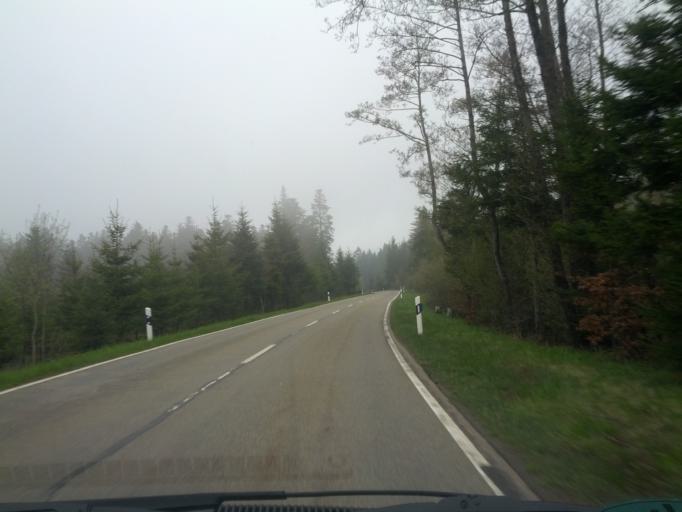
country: DE
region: Baden-Wuerttemberg
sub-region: Freiburg Region
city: Rickenbach
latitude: 47.6055
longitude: 8.0162
